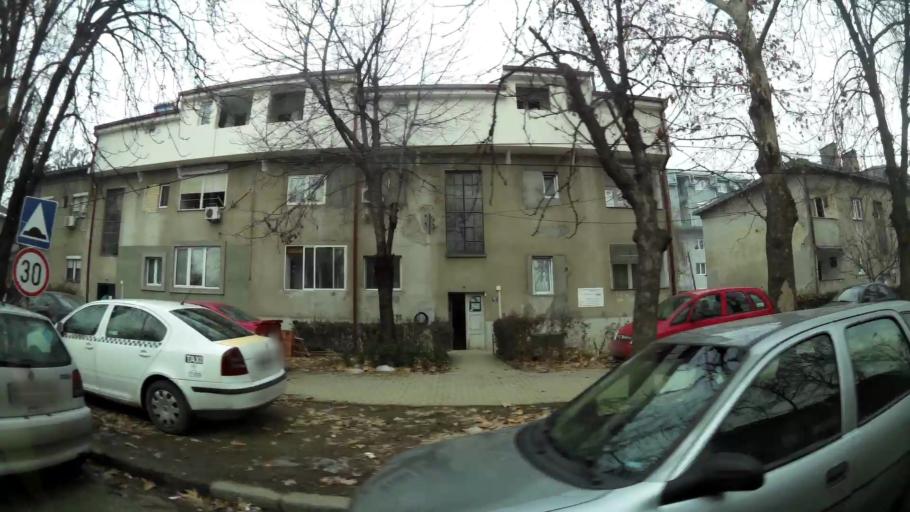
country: MK
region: Cair
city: Cair
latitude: 42.0041
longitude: 21.4665
